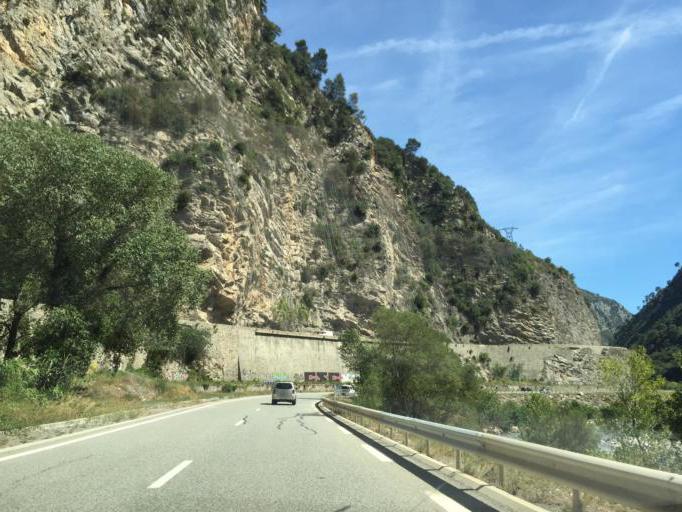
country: FR
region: Provence-Alpes-Cote d'Azur
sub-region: Departement des Alpes-Maritimes
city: Levens
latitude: 43.8774
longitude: 7.1918
